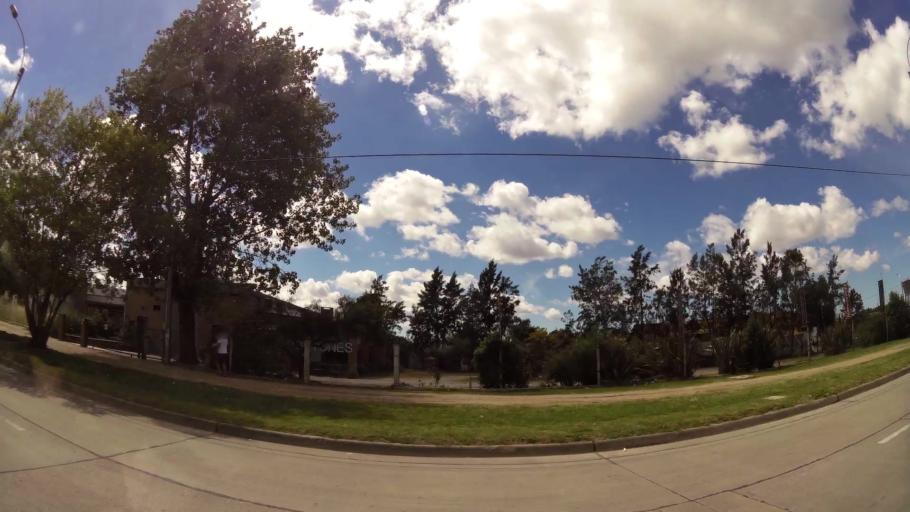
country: UY
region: Canelones
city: Paso de Carrasco
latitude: -34.8335
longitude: -56.1114
